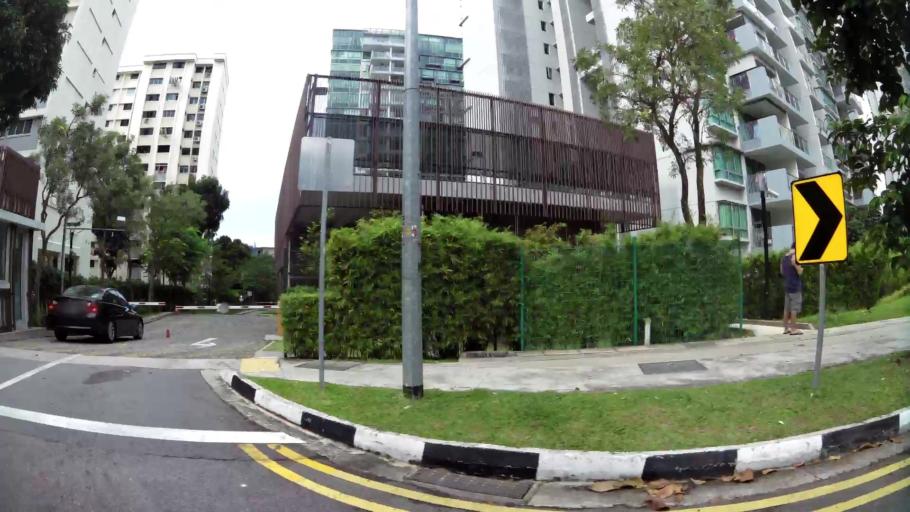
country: SG
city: Singapore
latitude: 1.3521
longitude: 103.8807
